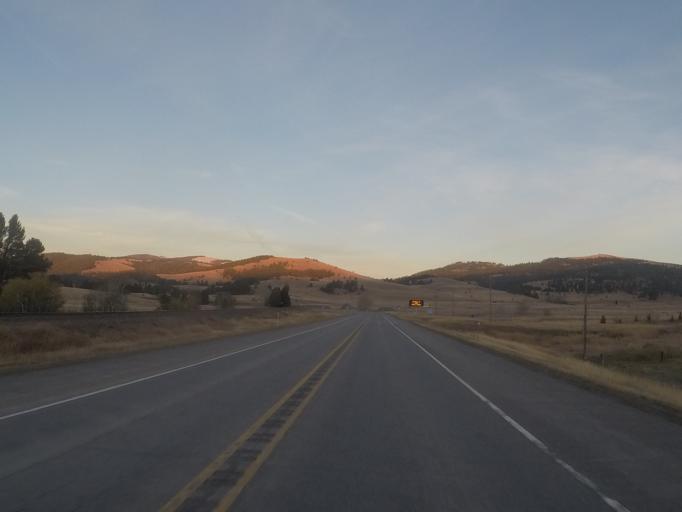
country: US
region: Montana
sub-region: Lewis and Clark County
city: Helena West Side
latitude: 46.5567
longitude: -112.4008
